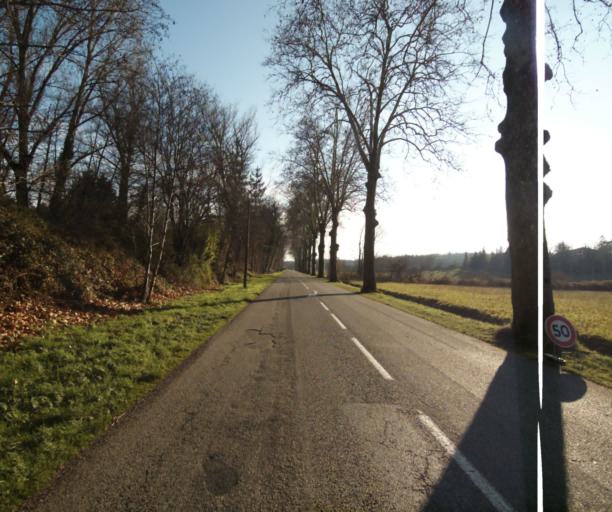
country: FR
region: Midi-Pyrenees
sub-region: Departement du Tarn-et-Garonne
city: Moissac
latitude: 44.1302
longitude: 1.1038
